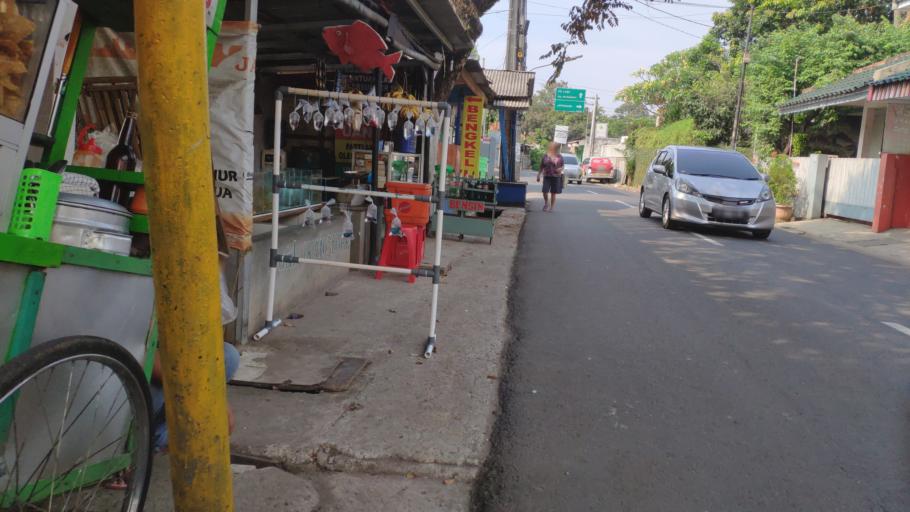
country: ID
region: West Java
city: Pamulang
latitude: -6.3179
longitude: 106.8160
